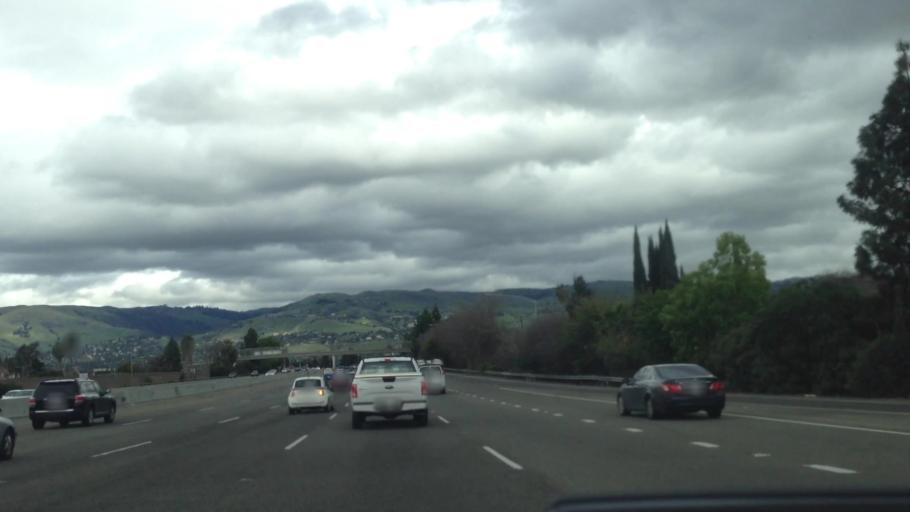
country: US
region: California
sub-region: Santa Clara County
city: Alum Rock
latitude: 37.3441
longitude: -121.8440
